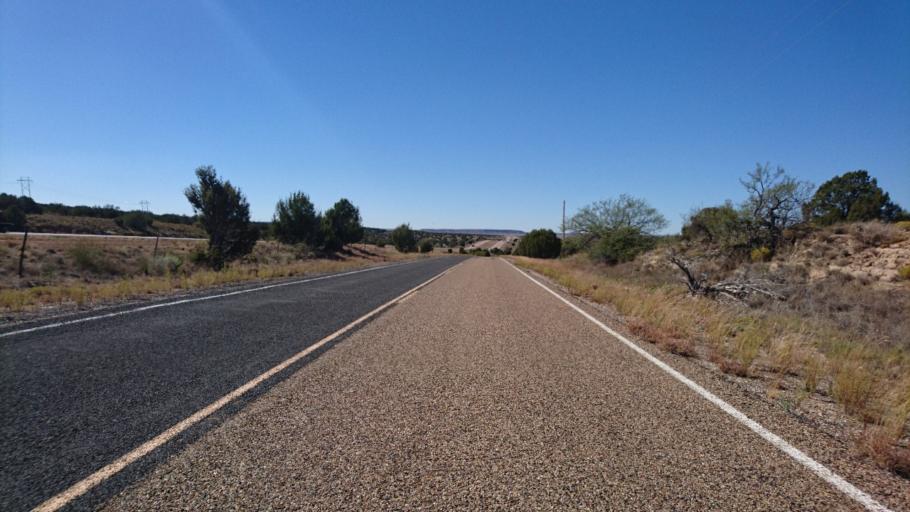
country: US
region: New Mexico
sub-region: Quay County
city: Tucumcari
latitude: 35.0668
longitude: -104.1871
